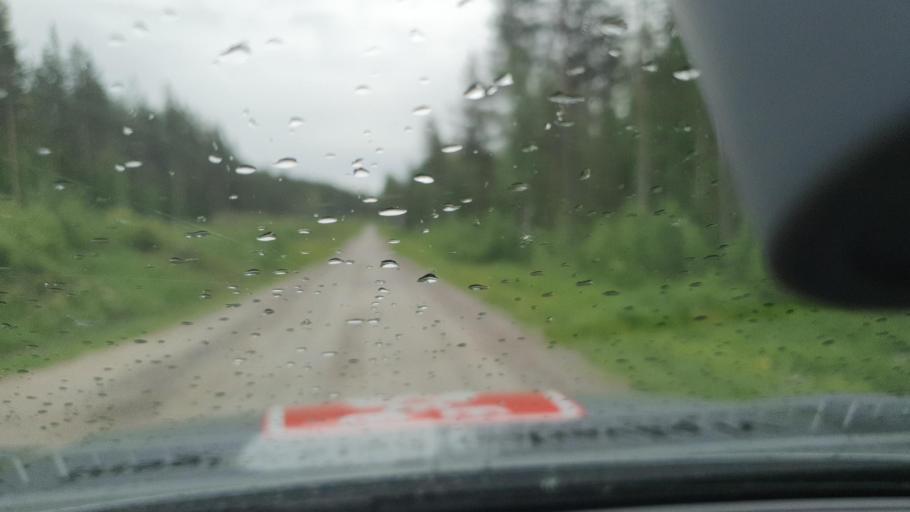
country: SE
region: Norrbotten
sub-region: Kalix Kommun
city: Rolfs
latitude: 66.0188
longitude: 23.1058
